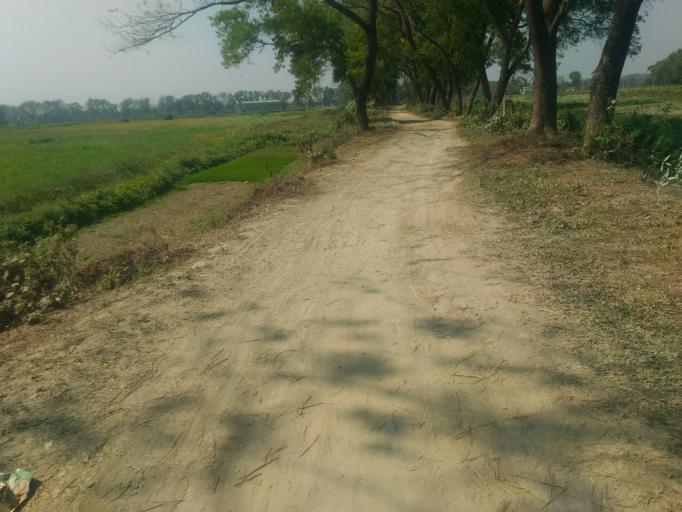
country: BD
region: Dhaka
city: Azimpur
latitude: 23.7841
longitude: 90.2339
